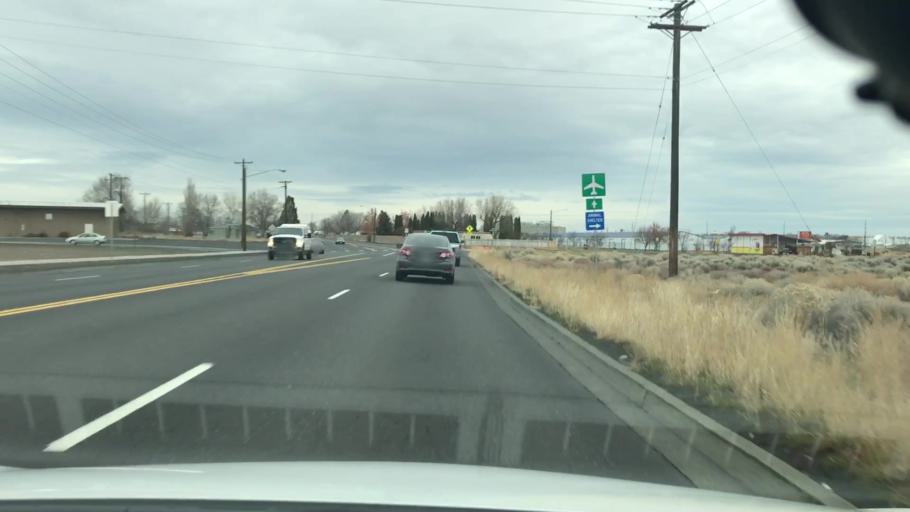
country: US
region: Washington
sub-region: Grant County
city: Moses Lake North
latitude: 47.1733
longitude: -119.3186
